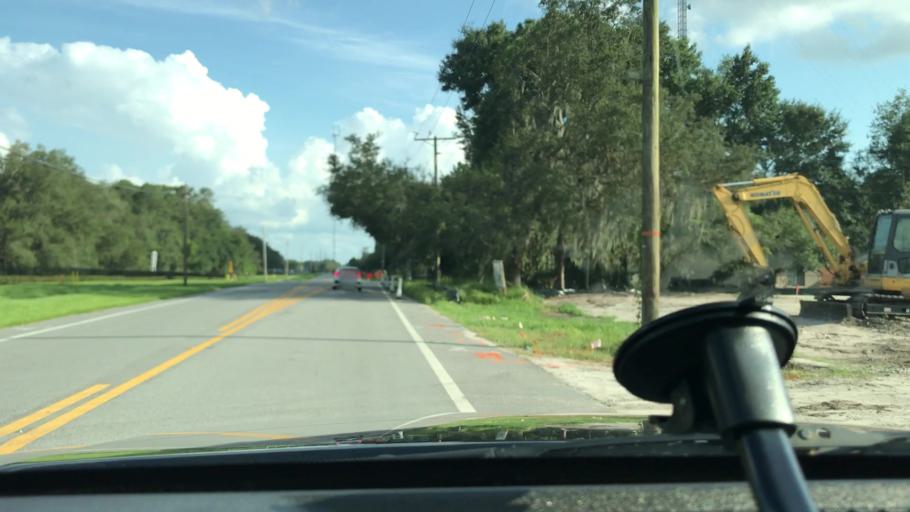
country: US
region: Florida
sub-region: Hillsborough County
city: Boyette
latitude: 27.8459
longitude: -82.2610
